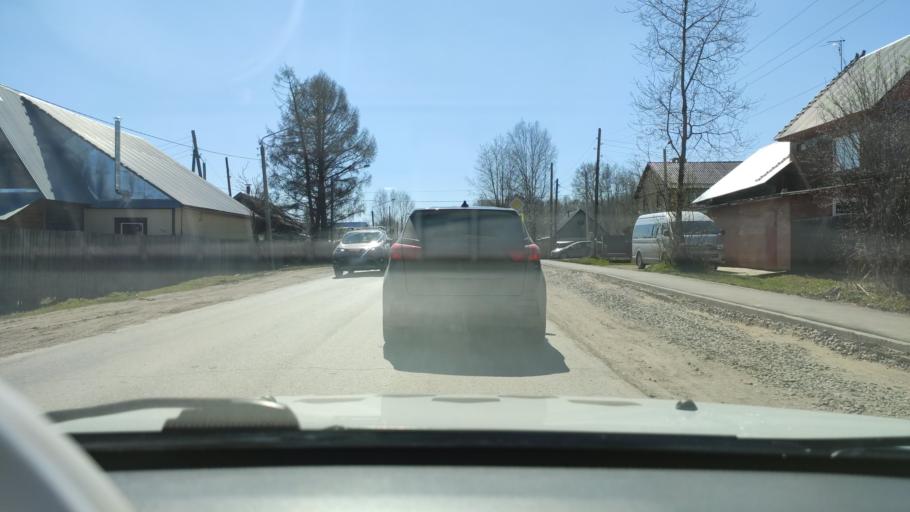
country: RU
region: Perm
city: Novyye Lyady
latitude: 58.0490
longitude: 56.5945
